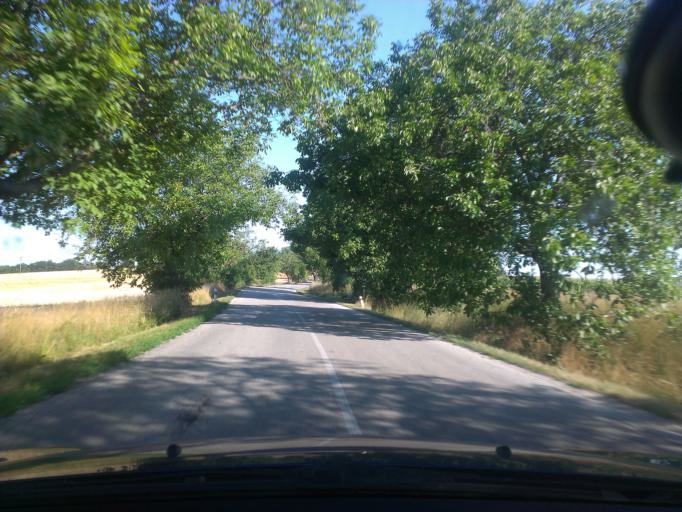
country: SK
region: Trnavsky
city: Vrbove
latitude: 48.6491
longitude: 17.7082
